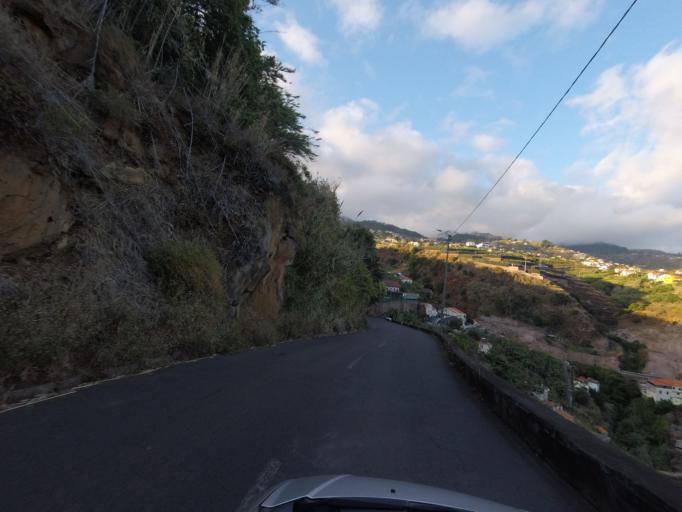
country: PT
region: Madeira
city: Ponta do Sol
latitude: 32.6889
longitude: -17.1099
